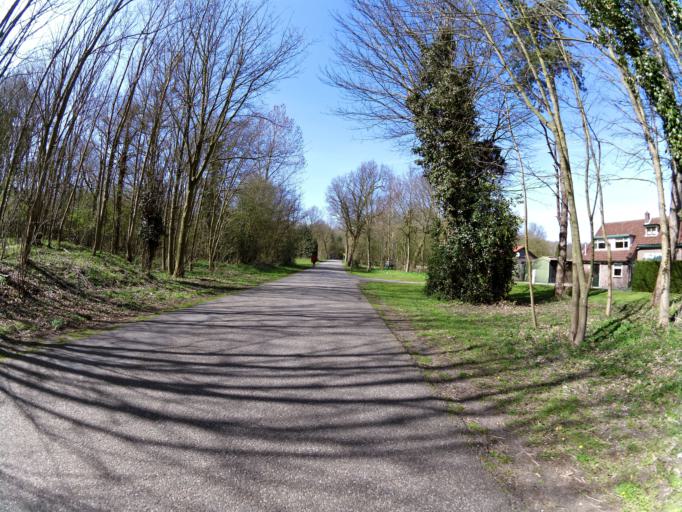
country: NL
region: South Holland
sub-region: Gemeente Hellevoetsluis
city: Nieuwenhoorn
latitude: 51.9054
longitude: 4.0783
